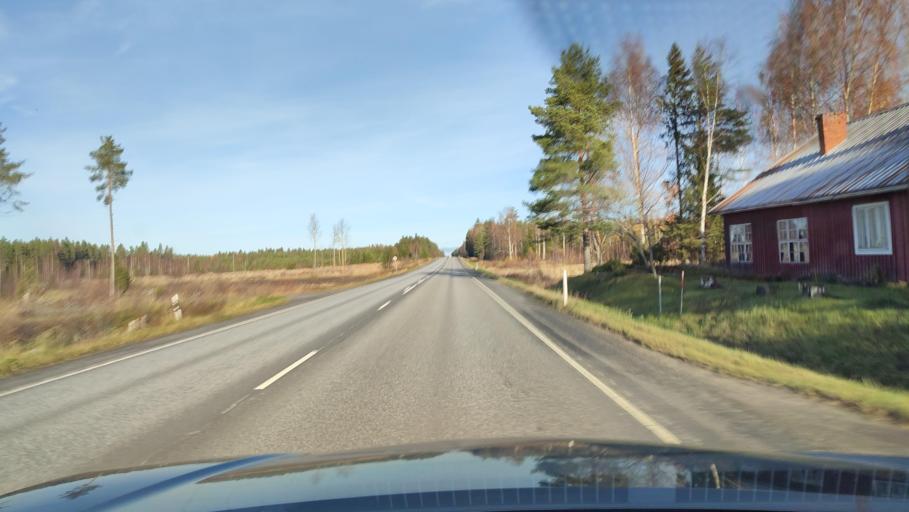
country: FI
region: Ostrobothnia
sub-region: Vaasa
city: Malax
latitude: 62.7818
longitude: 21.6649
